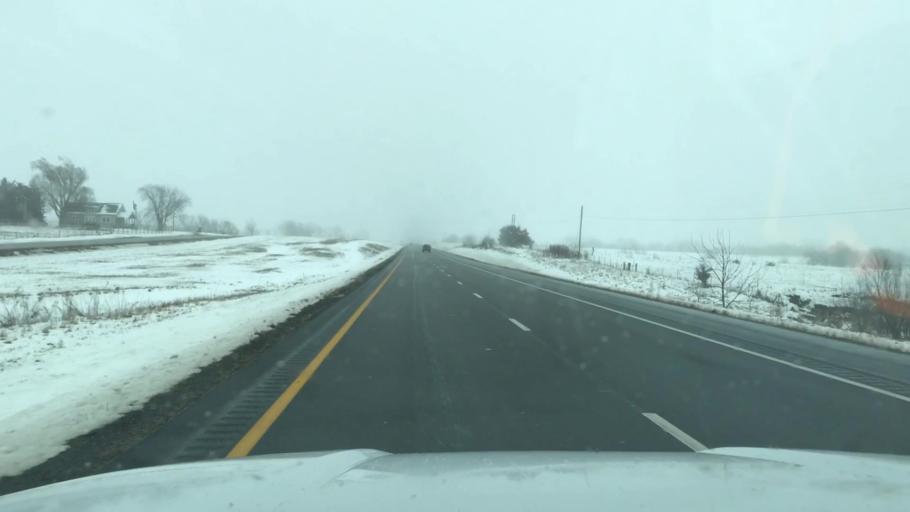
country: US
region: Missouri
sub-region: DeKalb County
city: Maysville
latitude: 39.7616
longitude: -94.4191
